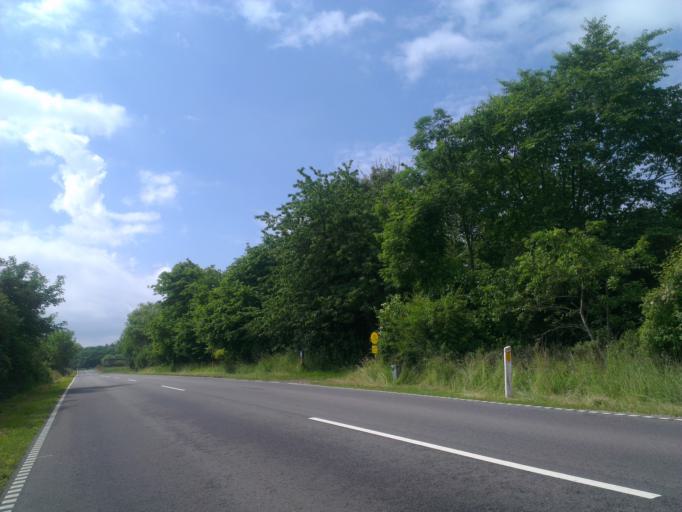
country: DK
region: Capital Region
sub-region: Frederikssund Kommune
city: Jaegerspris
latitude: 55.8818
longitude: 11.9549
